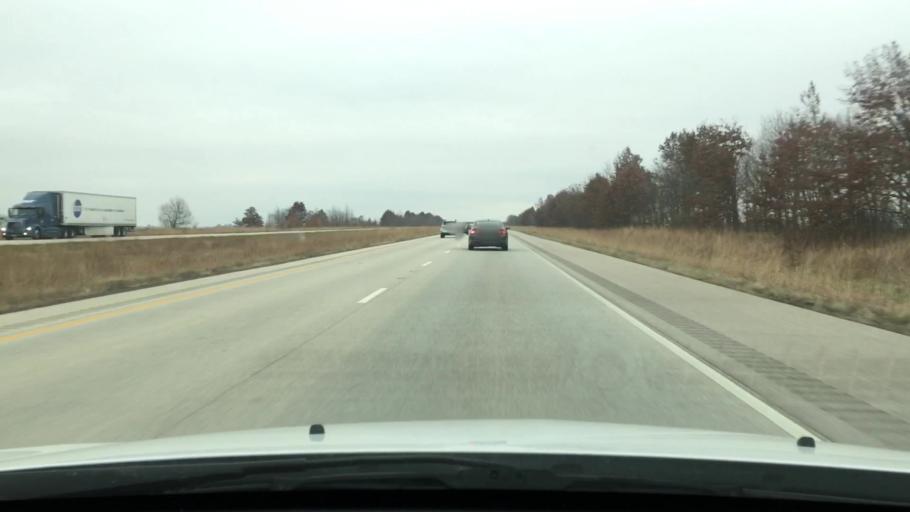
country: US
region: Illinois
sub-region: Sangamon County
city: New Berlin
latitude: 39.7407
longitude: -89.8574
